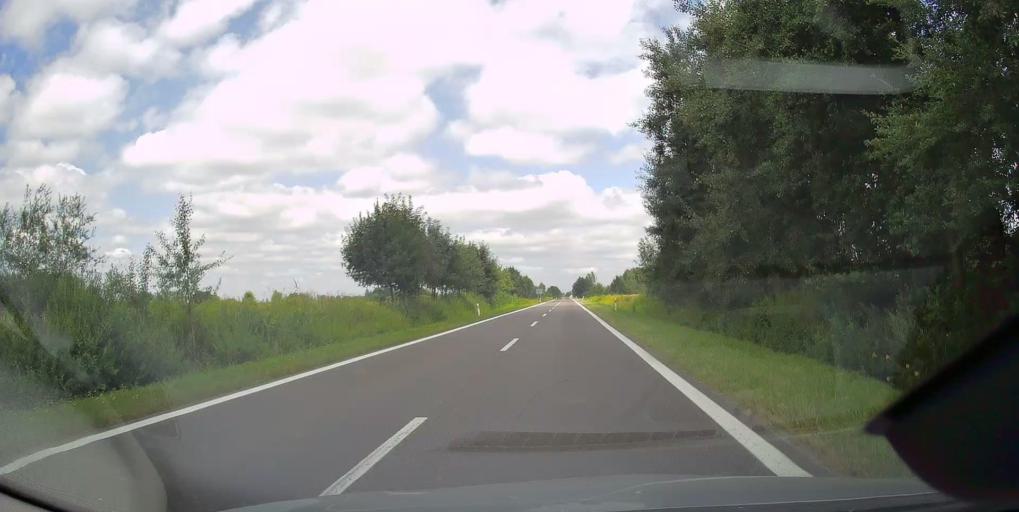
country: PL
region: Subcarpathian Voivodeship
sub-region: Powiat tarnobrzeski
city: Baranow Sandomierski
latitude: 50.4905
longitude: 21.5695
